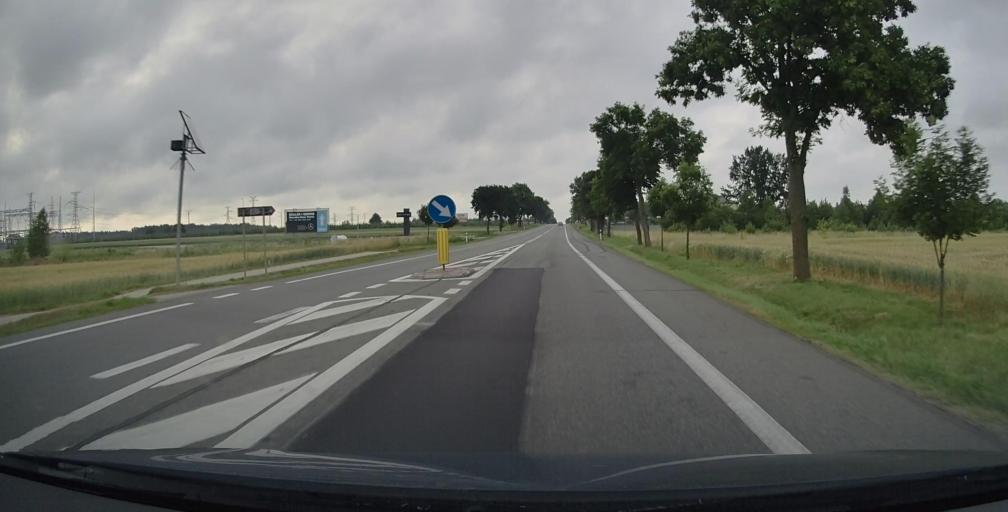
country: PL
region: Masovian Voivodeship
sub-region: Siedlce
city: Siedlce
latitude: 52.1281
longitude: 22.3389
